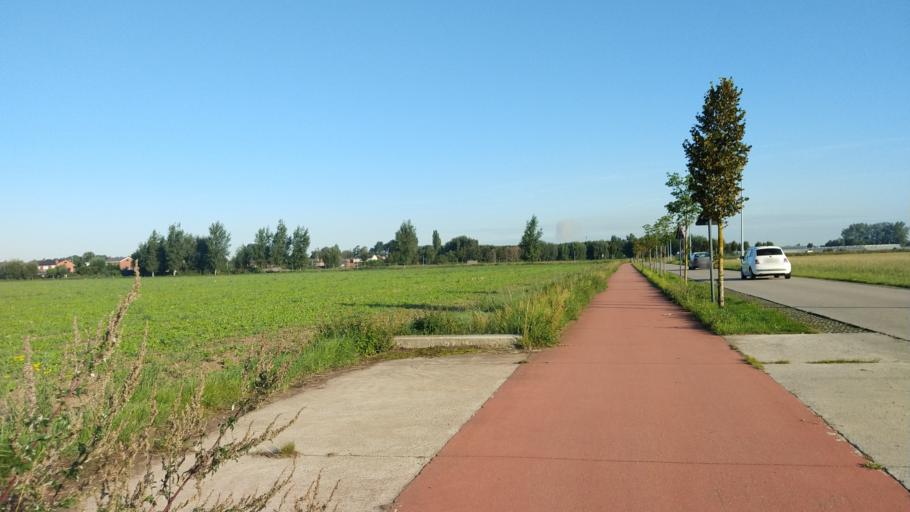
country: BE
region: Flanders
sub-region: Provincie Oost-Vlaanderen
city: Lochristi
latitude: 51.0854
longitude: 3.8630
